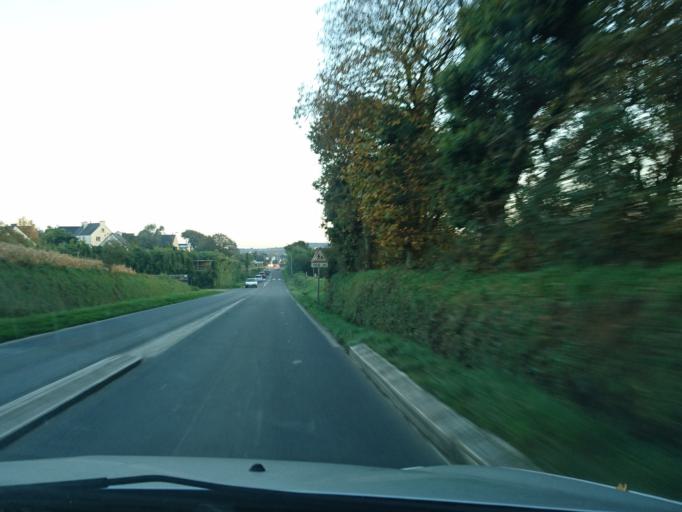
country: FR
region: Brittany
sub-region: Departement du Finistere
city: Saint-Renan
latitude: 48.4425
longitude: -4.6216
